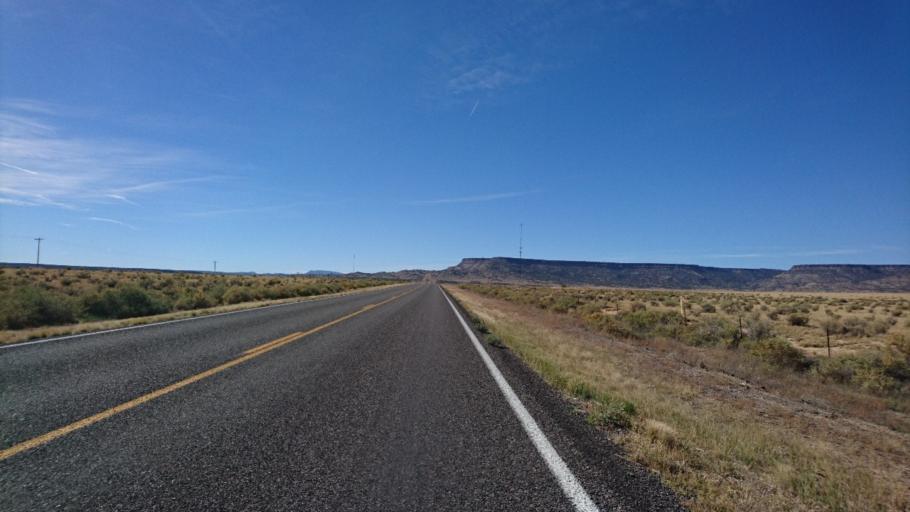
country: US
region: New Mexico
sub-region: Cibola County
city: Skyline-Ganipa
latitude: 35.0825
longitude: -107.6235
